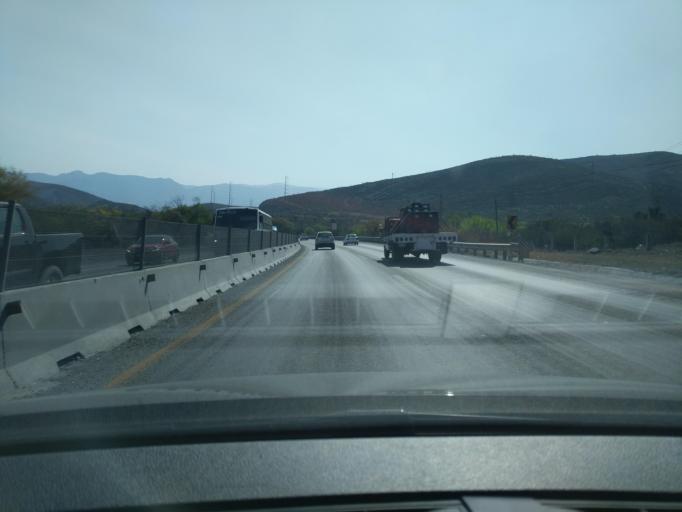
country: MX
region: Nuevo Leon
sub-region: Garcia
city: Los Parques
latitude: 25.7618
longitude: -100.4953
